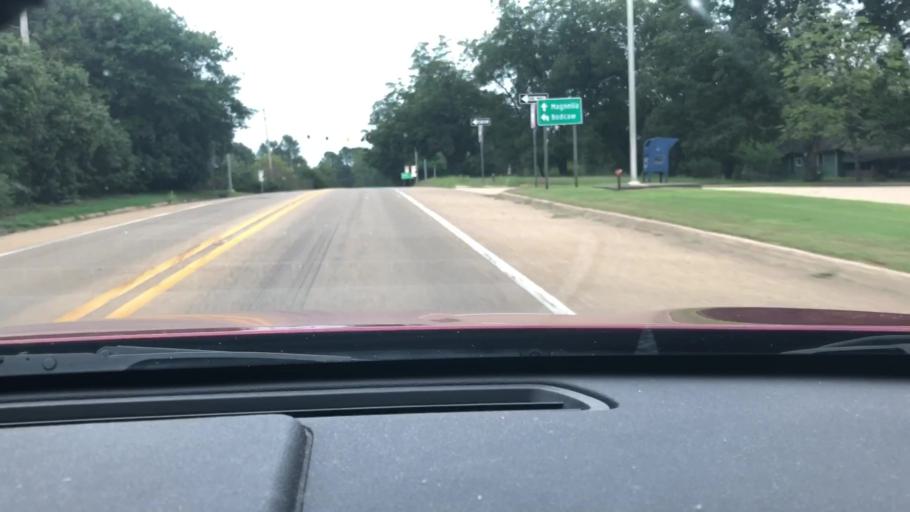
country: US
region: Arkansas
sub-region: Lafayette County
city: Stamps
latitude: 33.3585
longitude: -93.4358
